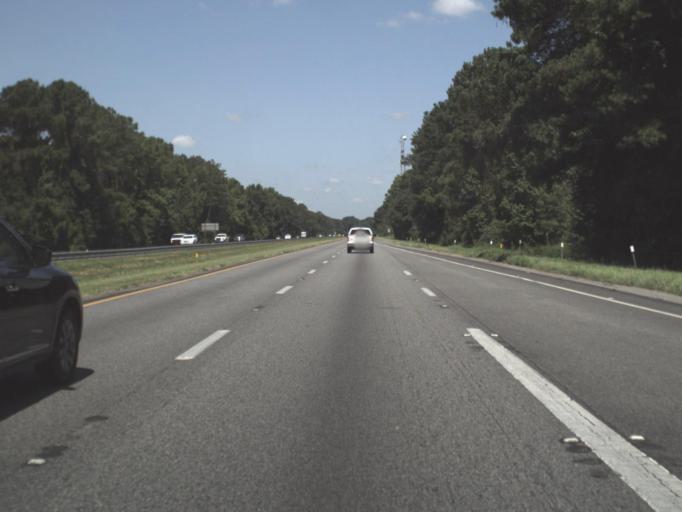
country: US
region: Florida
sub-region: Madison County
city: Madison
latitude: 30.4346
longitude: -83.6329
